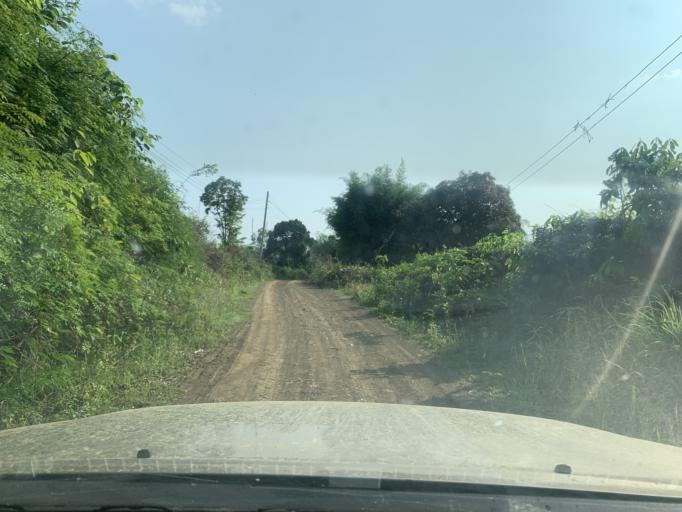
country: TH
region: Uttaradit
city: Ban Khok
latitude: 18.2843
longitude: 101.3173
